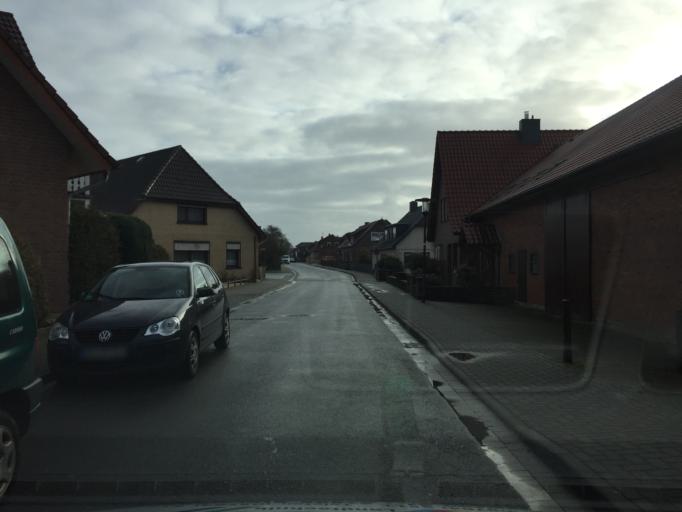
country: DE
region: Lower Saxony
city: Sulingen
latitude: 52.6807
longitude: 8.8070
